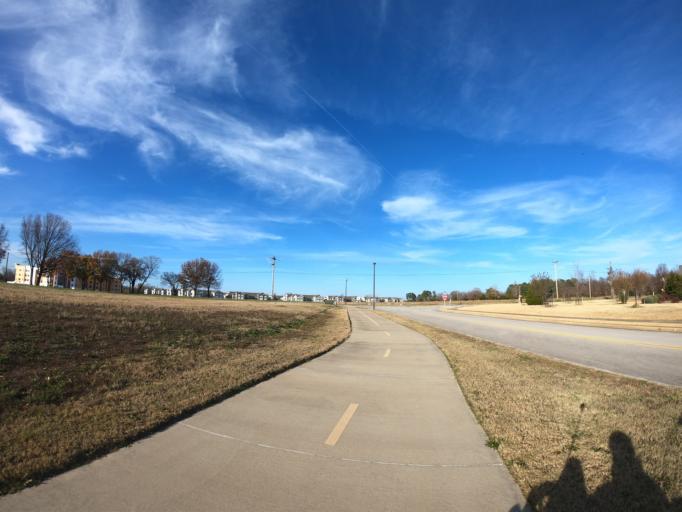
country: US
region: Arkansas
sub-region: Benton County
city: Bentonville
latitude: 36.3270
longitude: -94.1764
